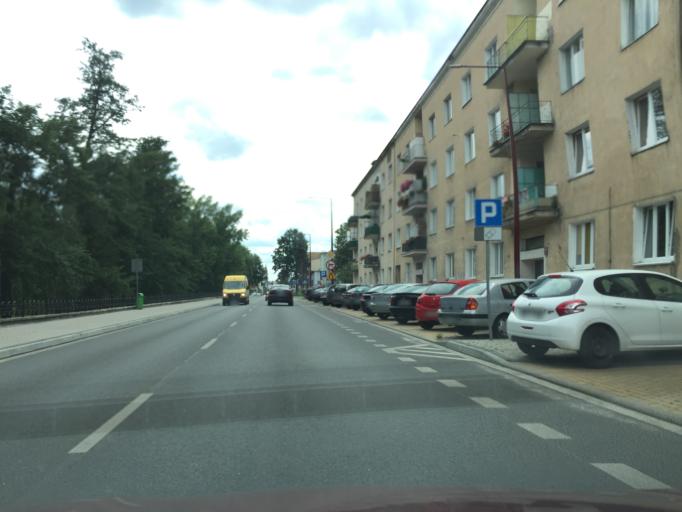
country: PL
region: Greater Poland Voivodeship
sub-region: Kalisz
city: Kalisz
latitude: 51.7577
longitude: 18.0934
